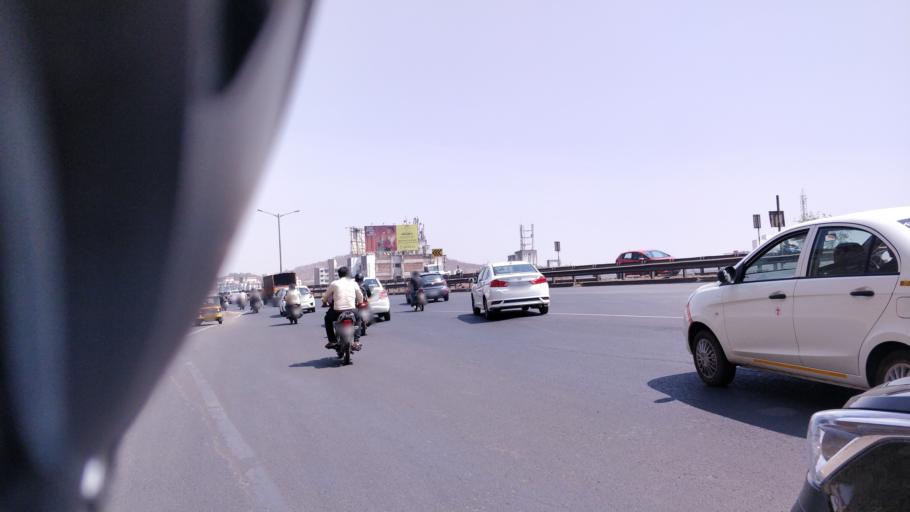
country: IN
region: Maharashtra
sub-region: Pune Division
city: Shivaji Nagar
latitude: 18.5374
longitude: 73.7810
